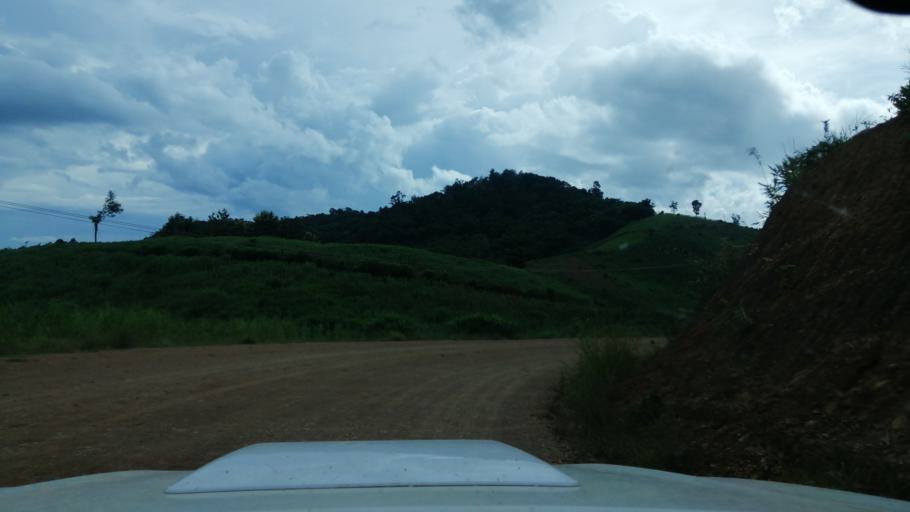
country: TH
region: Nan
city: Song Khwae
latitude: 19.5466
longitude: 100.7011
